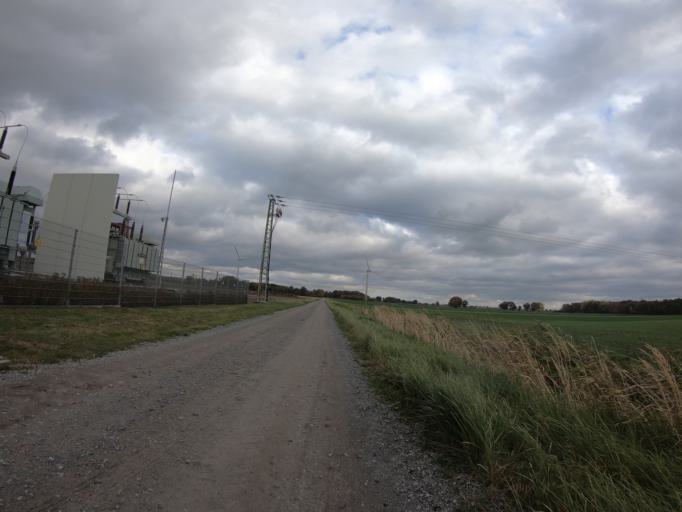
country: DE
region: Lower Saxony
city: Vordorf
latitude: 52.3789
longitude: 10.4961
